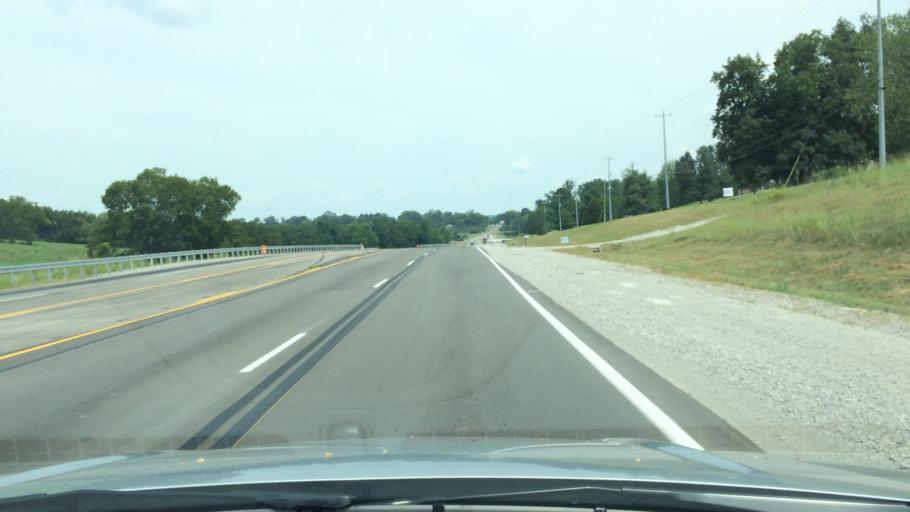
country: US
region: Tennessee
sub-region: Giles County
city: Pulaski
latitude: 35.1640
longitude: -87.0115
